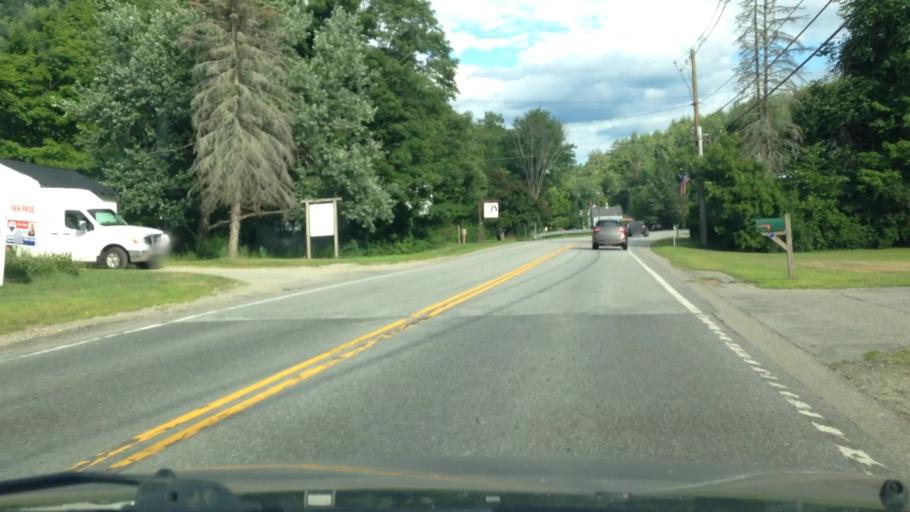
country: US
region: New Hampshire
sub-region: Cheshire County
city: Marlborough
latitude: 42.9115
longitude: -72.2222
